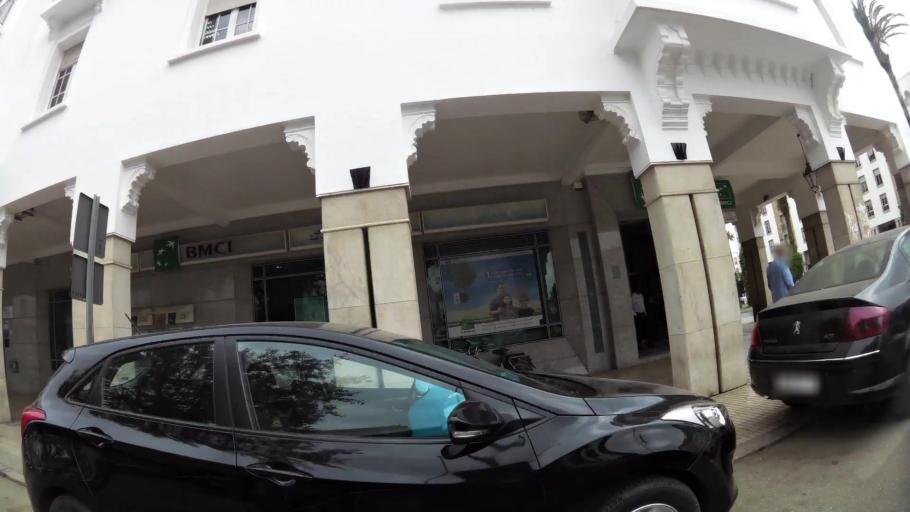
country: MA
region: Rabat-Sale-Zemmour-Zaer
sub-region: Rabat
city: Rabat
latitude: 34.0171
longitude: -6.8359
